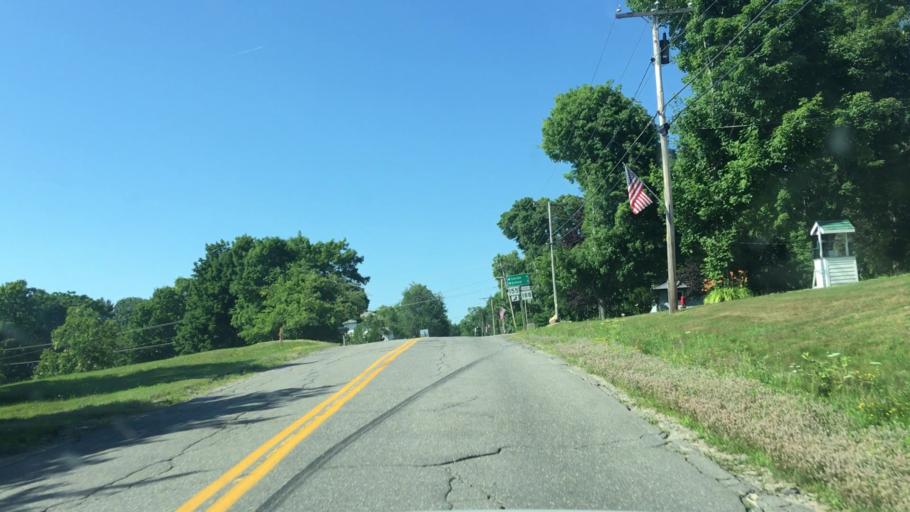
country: US
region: Maine
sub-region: Penobscot County
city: Enfield
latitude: 45.2478
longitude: -68.5659
